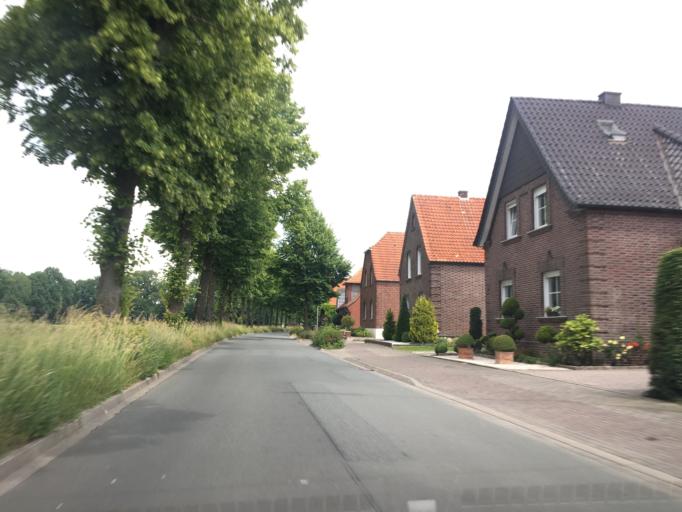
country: DE
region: North Rhine-Westphalia
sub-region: Regierungsbezirk Munster
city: Laer
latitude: 52.1034
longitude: 7.3956
